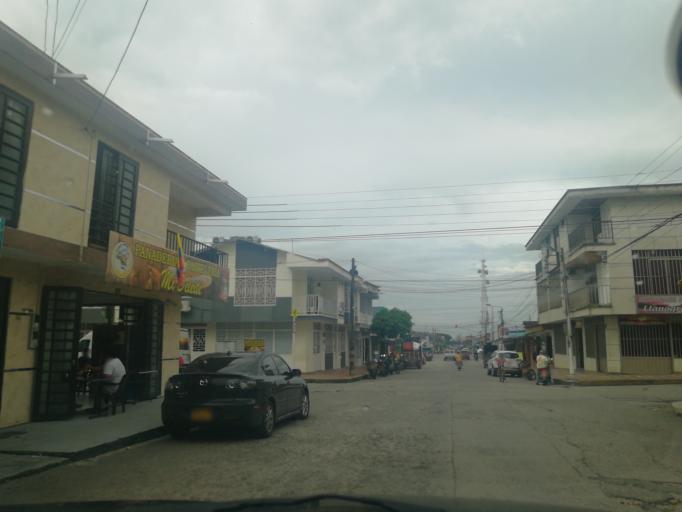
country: CO
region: Meta
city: Acacias
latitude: 3.9864
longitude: -73.7675
